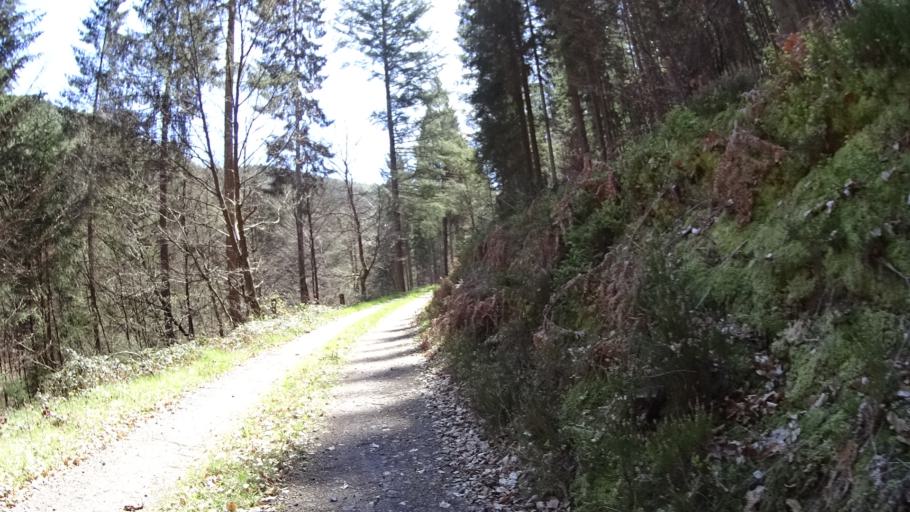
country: DE
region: Rheinland-Pfalz
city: Esthal
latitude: 49.3326
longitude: 7.9892
